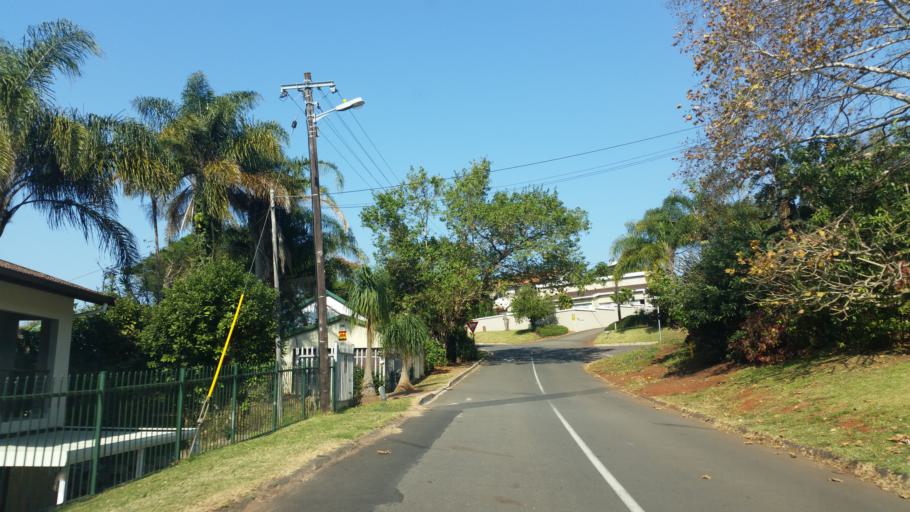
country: ZA
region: KwaZulu-Natal
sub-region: eThekwini Metropolitan Municipality
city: Berea
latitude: -29.8512
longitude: 30.9006
